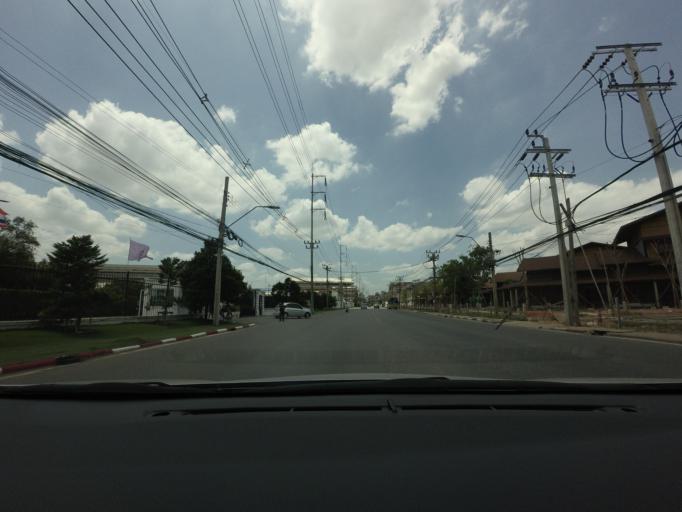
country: TH
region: Samut Prakan
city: Samut Prakan
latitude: 13.5818
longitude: 100.5933
